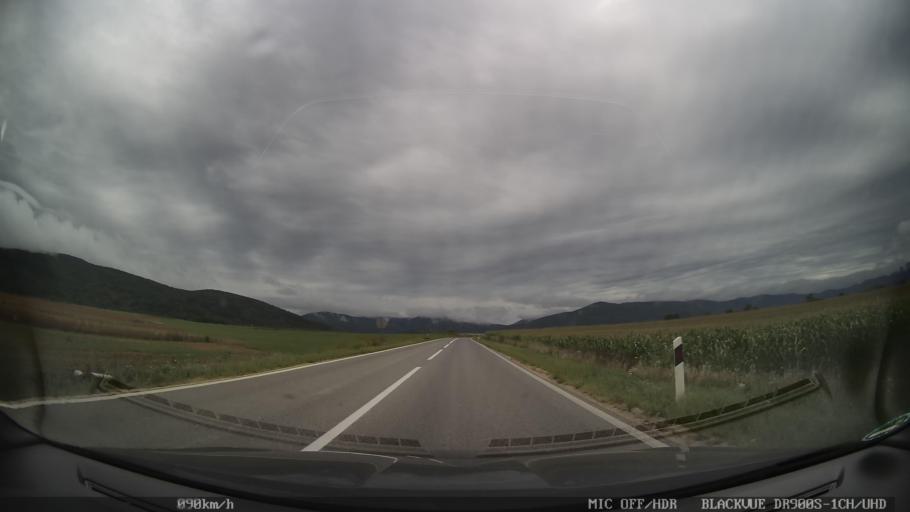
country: HR
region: Licko-Senjska
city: Otocac
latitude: 44.8561
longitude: 15.2768
